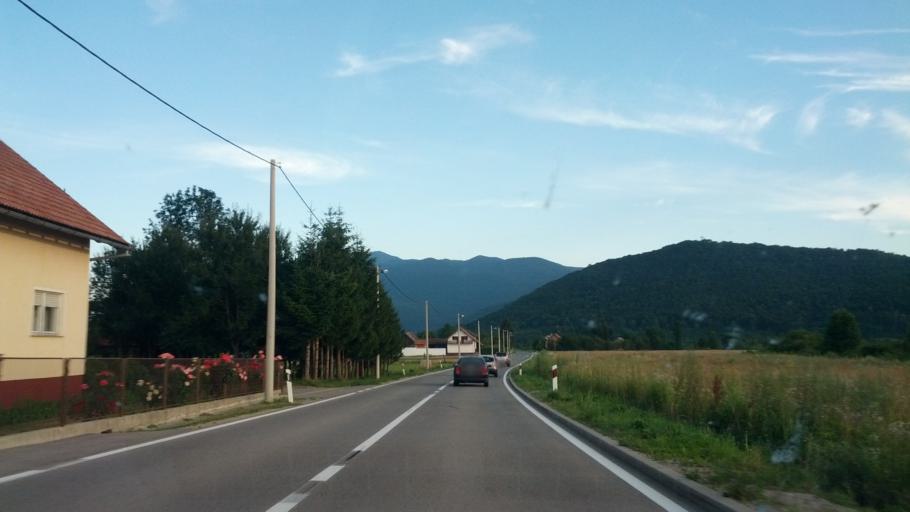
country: BA
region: Federation of Bosnia and Herzegovina
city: Izacic
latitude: 44.9017
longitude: 15.7242
